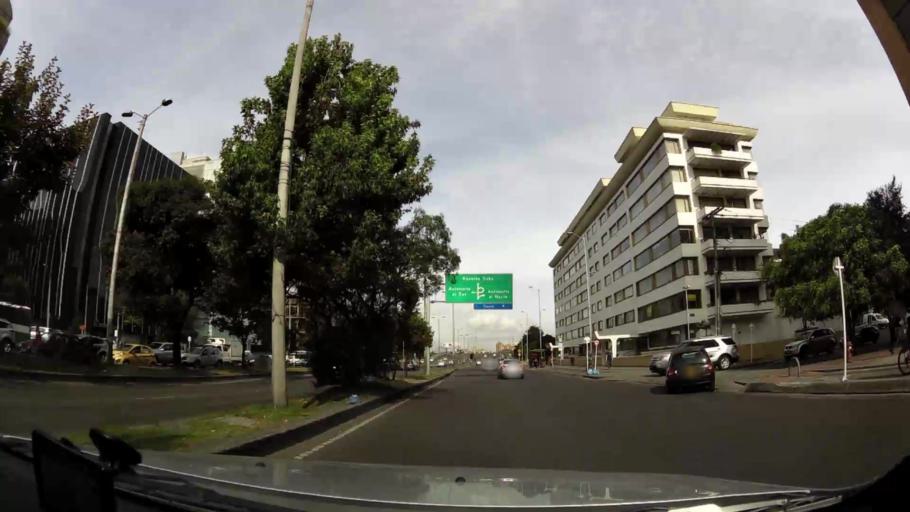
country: CO
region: Bogota D.C.
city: Barrio San Luis
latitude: 4.6865
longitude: -74.0545
